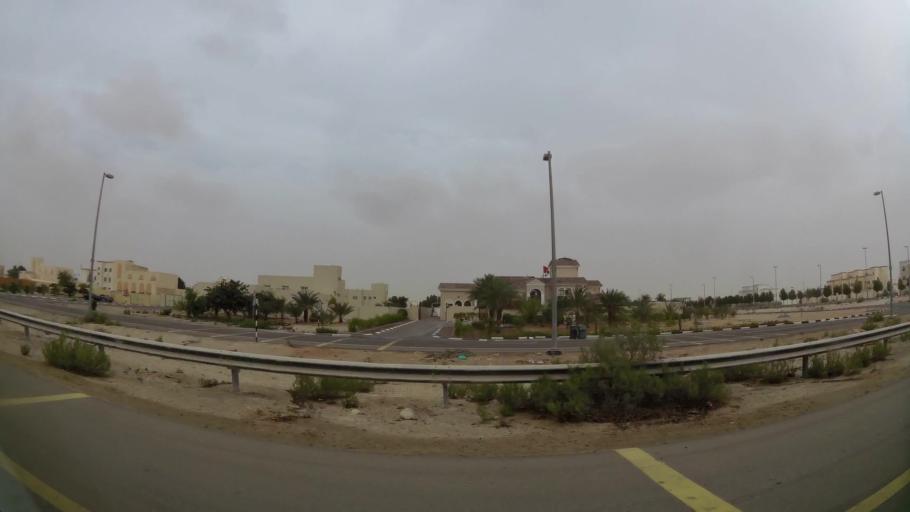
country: AE
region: Abu Dhabi
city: Abu Dhabi
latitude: 24.3852
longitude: 54.6943
